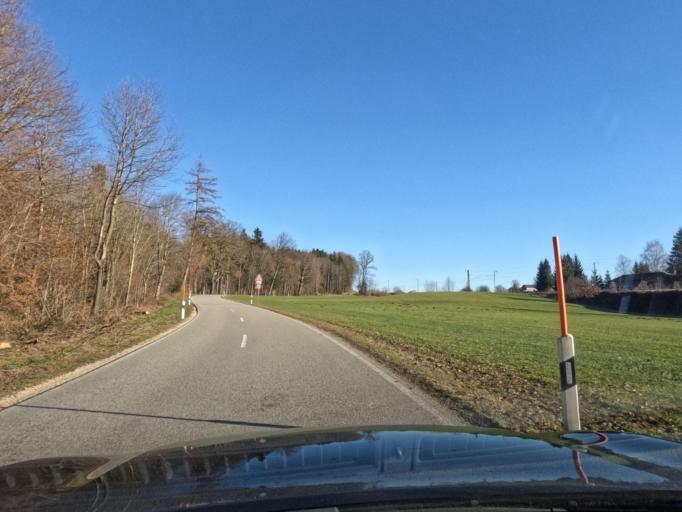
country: DE
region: Bavaria
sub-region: Upper Bavaria
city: Surberg
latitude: 47.8767
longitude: 12.6738
